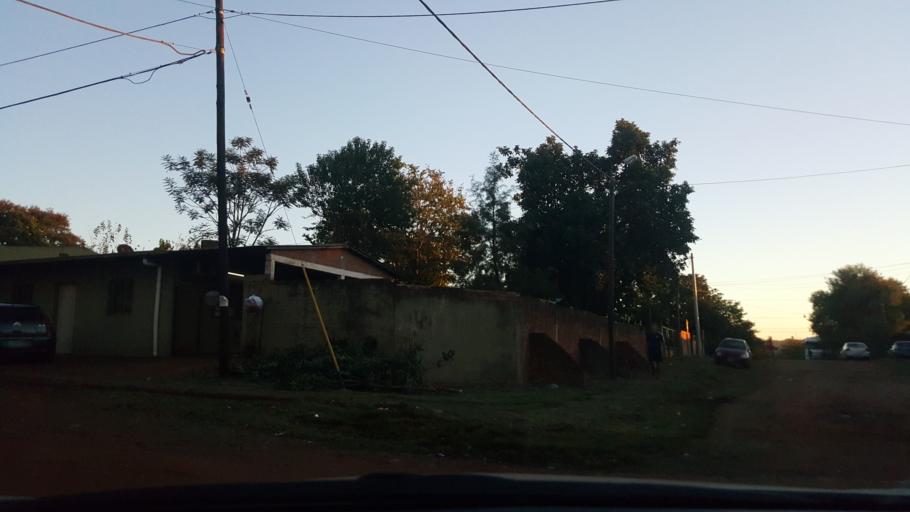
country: AR
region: Misiones
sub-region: Departamento de Capital
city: Posadas
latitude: -27.4230
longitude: -55.9023
